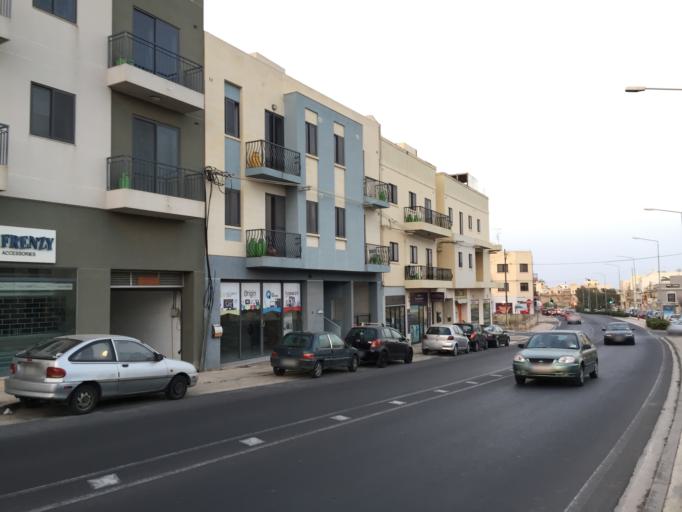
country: MT
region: Haz-Zabbar
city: Zabbar
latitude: 35.8712
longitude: 14.5338
